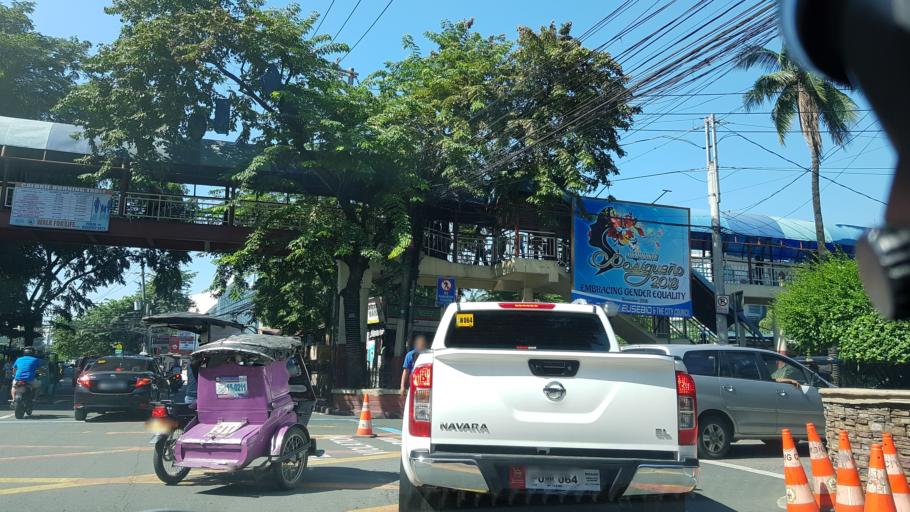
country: PH
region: Calabarzon
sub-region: Province of Rizal
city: Pateros
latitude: 14.5598
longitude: 121.0807
